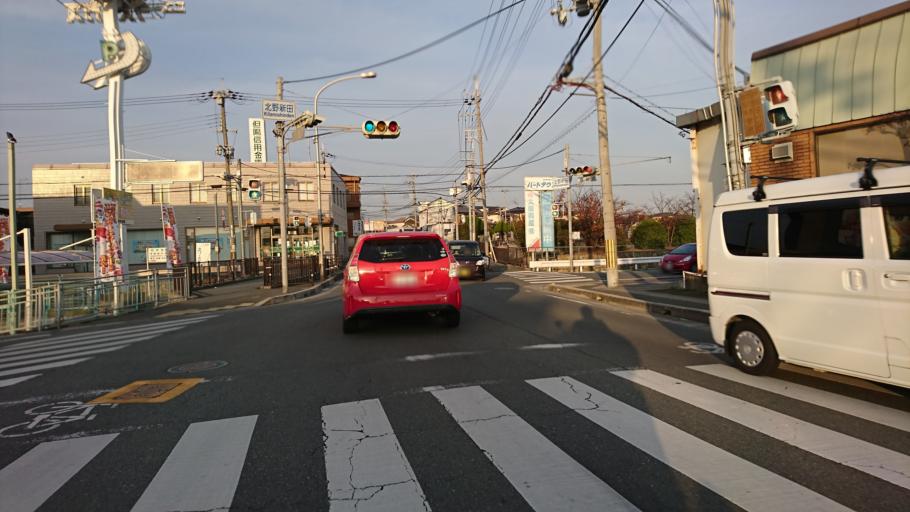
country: JP
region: Hyogo
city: Kakogawacho-honmachi
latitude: 34.7581
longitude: 134.8740
